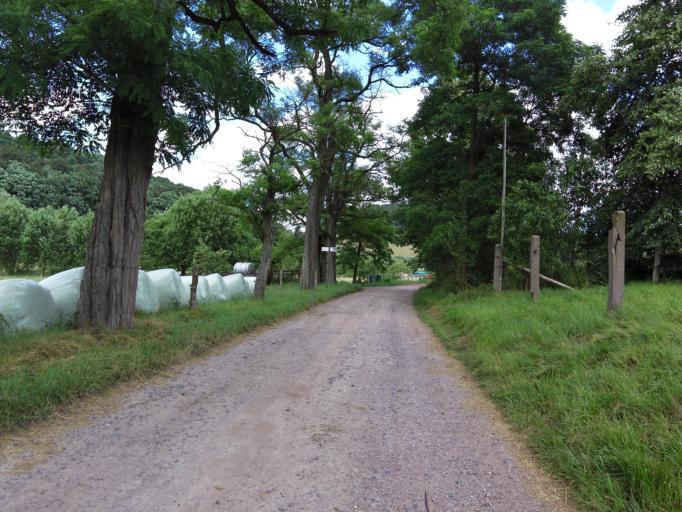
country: DE
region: Thuringia
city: Krauthausen
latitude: 50.9978
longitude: 10.2187
